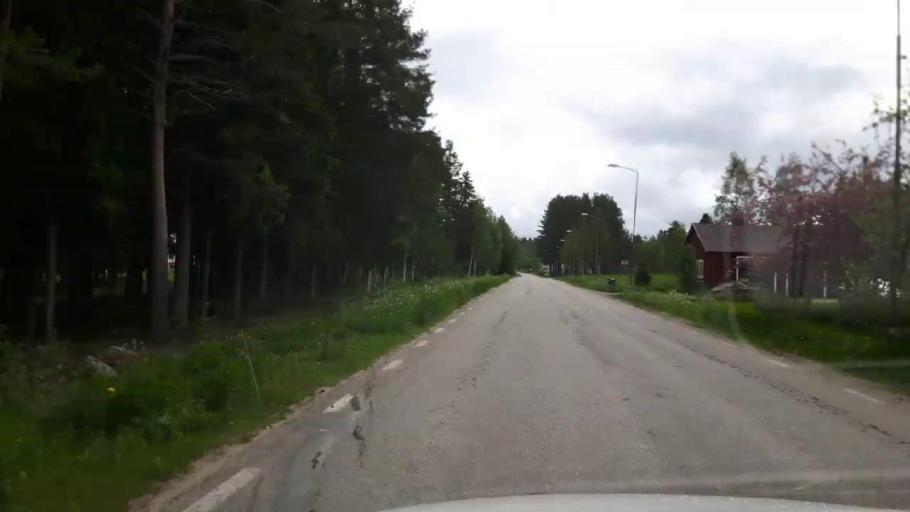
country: SE
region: Gaevleborg
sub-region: Ovanakers Kommun
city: Alfta
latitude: 61.3402
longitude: 15.9437
